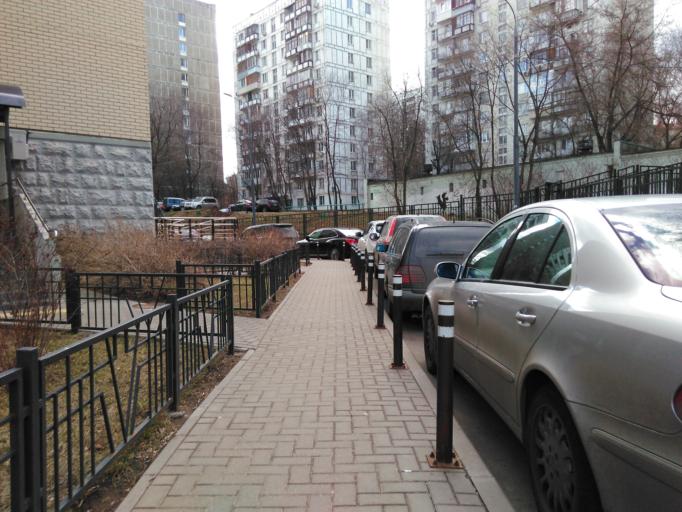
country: RU
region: Moscow
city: Mar'ina Roshcha
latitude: 55.8064
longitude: 37.6422
